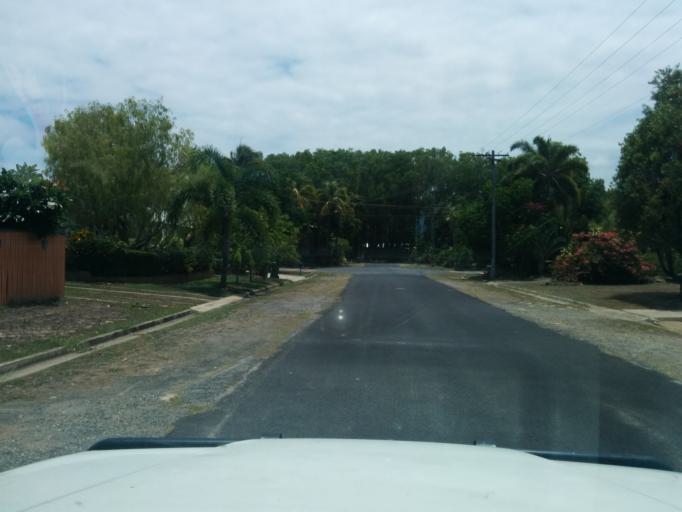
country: AU
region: Queensland
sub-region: Cairns
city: Yorkeys Knob
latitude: -16.8485
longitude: 145.7379
